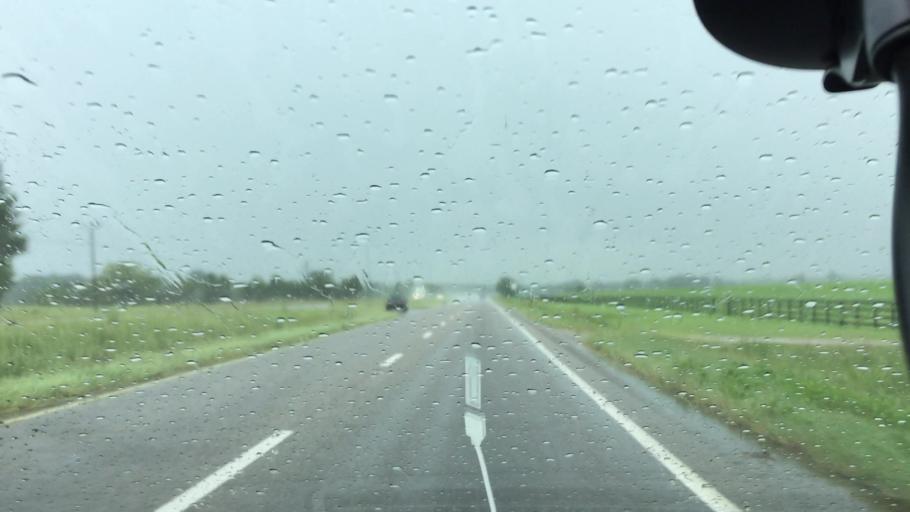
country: US
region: Alabama
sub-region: Montgomery County
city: Pike Road
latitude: 32.2365
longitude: -86.1275
